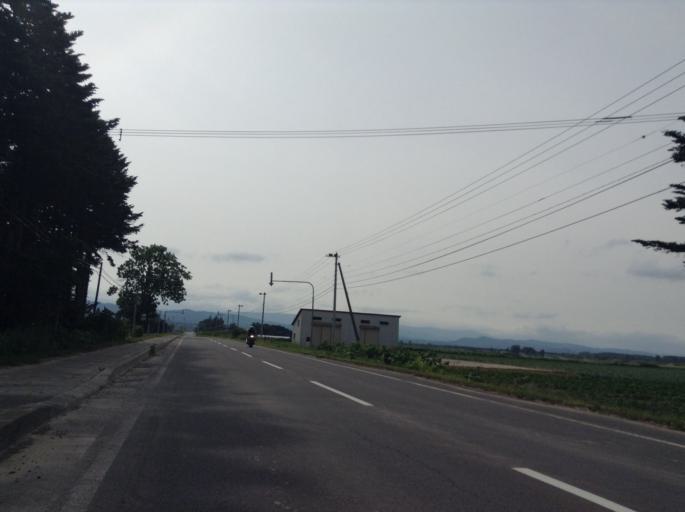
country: JP
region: Hokkaido
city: Nayoro
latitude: 44.4390
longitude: 142.3945
